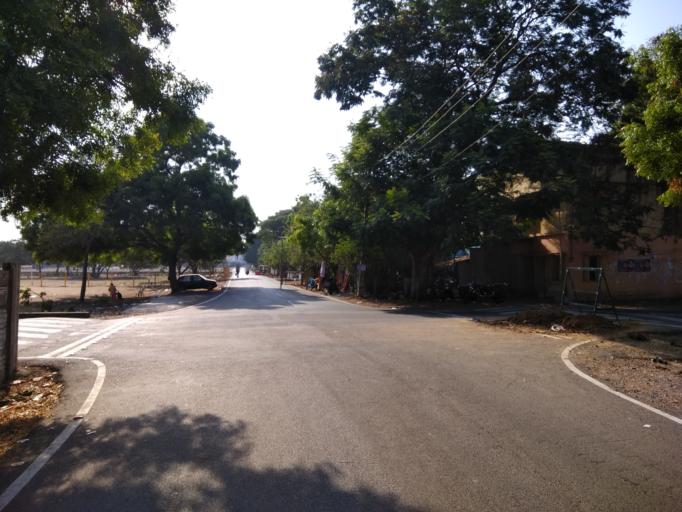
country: IN
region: Tamil Nadu
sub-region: Kancheepuram
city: Saint Thomas Mount
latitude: 13.0149
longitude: 80.1880
